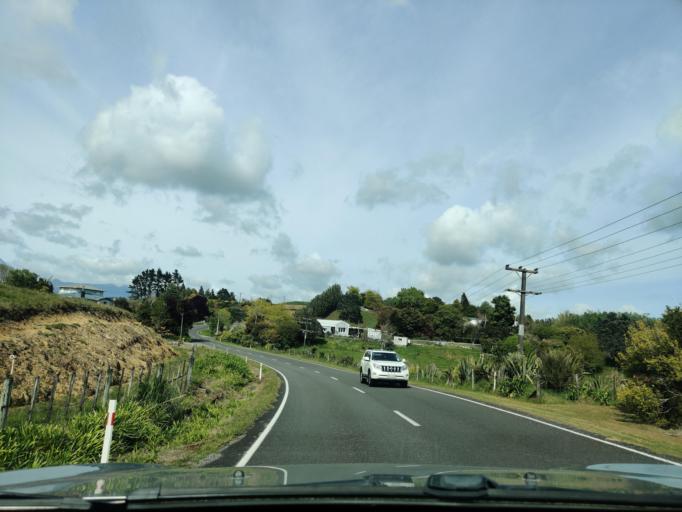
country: NZ
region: Taranaki
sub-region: New Plymouth District
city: New Plymouth
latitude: -39.0947
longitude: 174.1035
